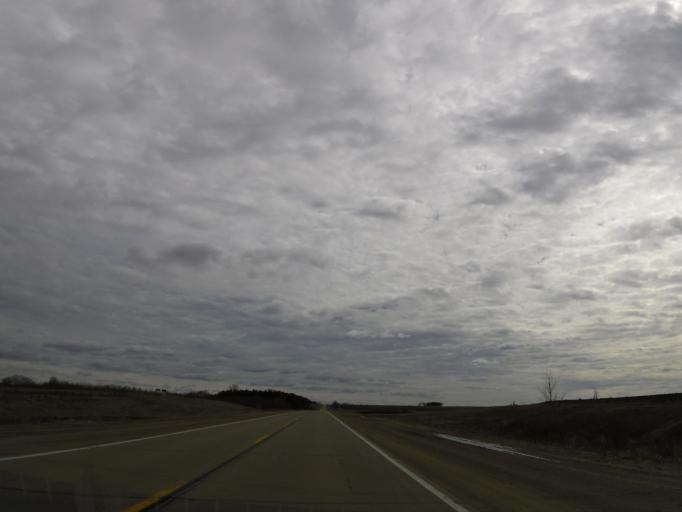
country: US
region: Iowa
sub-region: Howard County
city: Cresco
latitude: 43.3935
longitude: -92.2983
